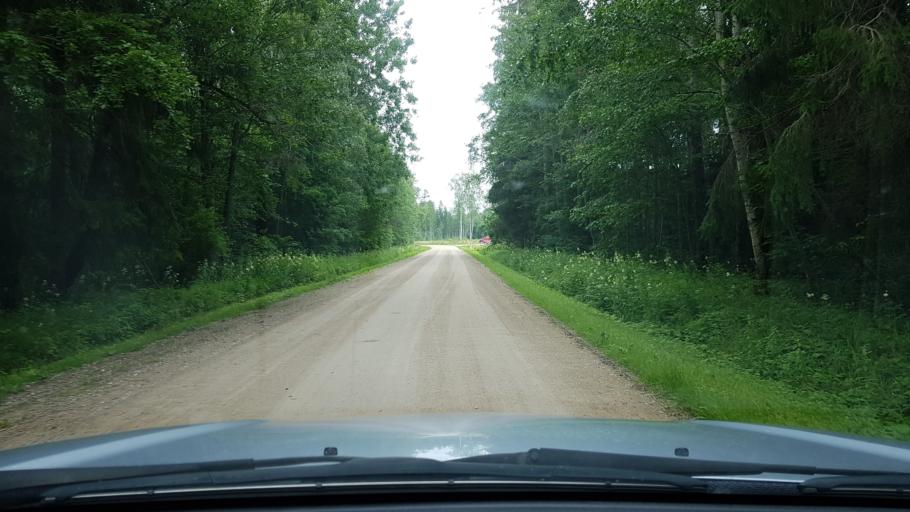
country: EE
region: Ida-Virumaa
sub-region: Narva-Joesuu linn
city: Narva-Joesuu
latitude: 59.3611
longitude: 28.0509
